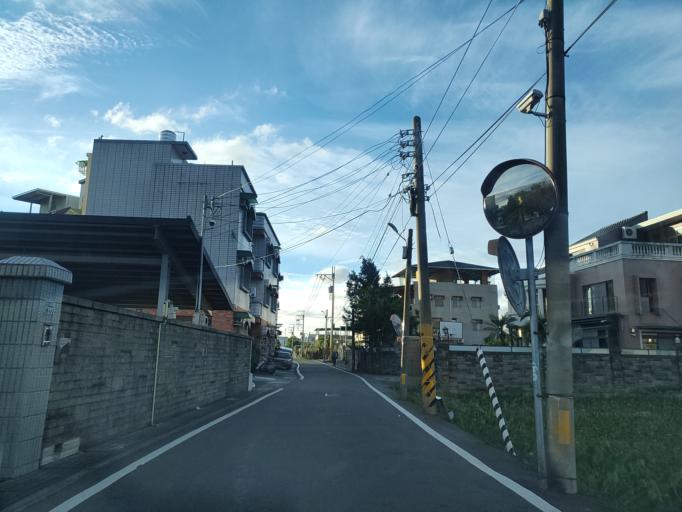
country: TW
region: Taiwan
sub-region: Miaoli
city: Miaoli
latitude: 24.5581
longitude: 120.8316
